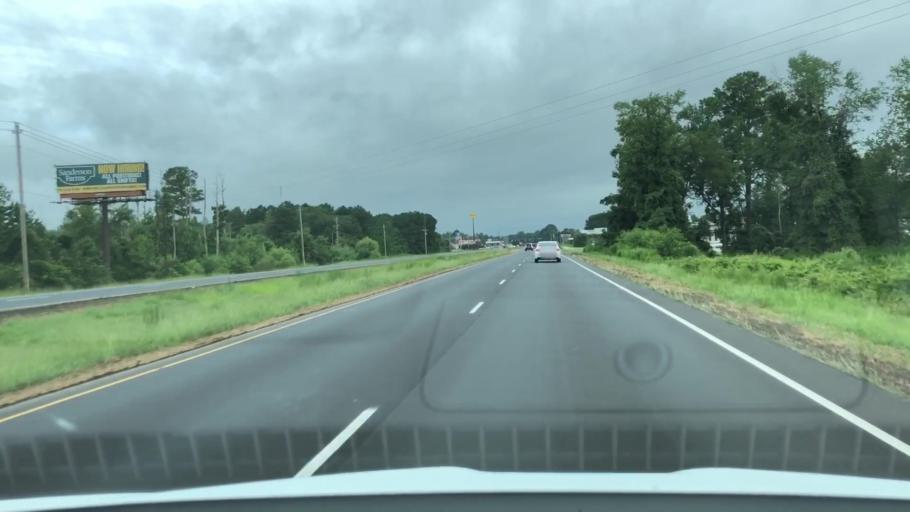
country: US
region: North Carolina
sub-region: Lenoir County
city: Kinston
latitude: 35.2494
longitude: -77.5953
